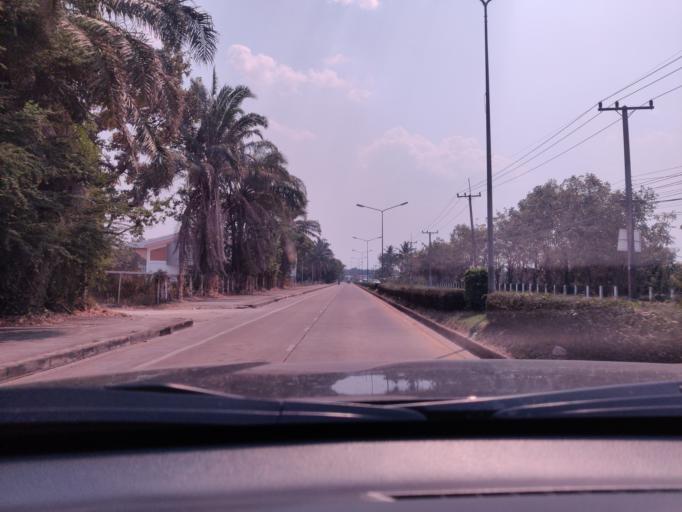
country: TH
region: Sisaket
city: Si Sa Ket
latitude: 15.1039
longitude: 104.3152
